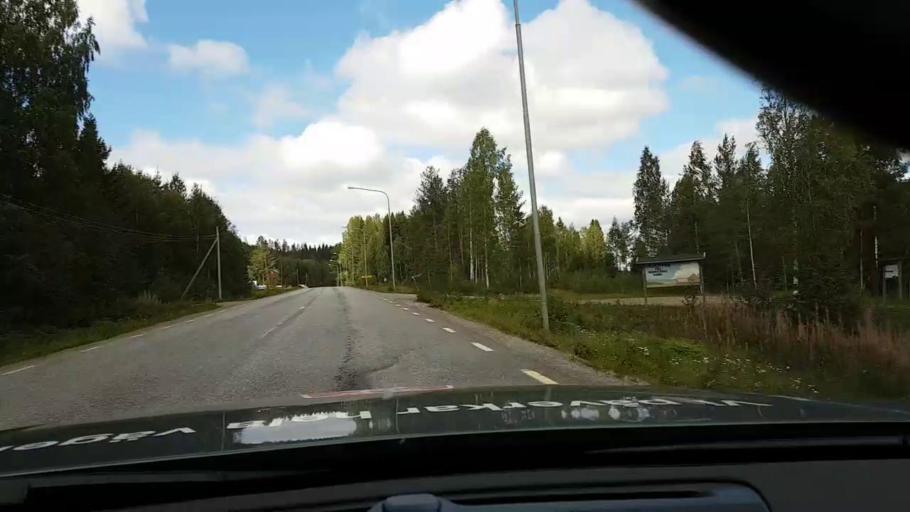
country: SE
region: Vaesternorrland
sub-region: OErnskoeldsviks Kommun
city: Bredbyn
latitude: 63.4886
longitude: 18.0838
